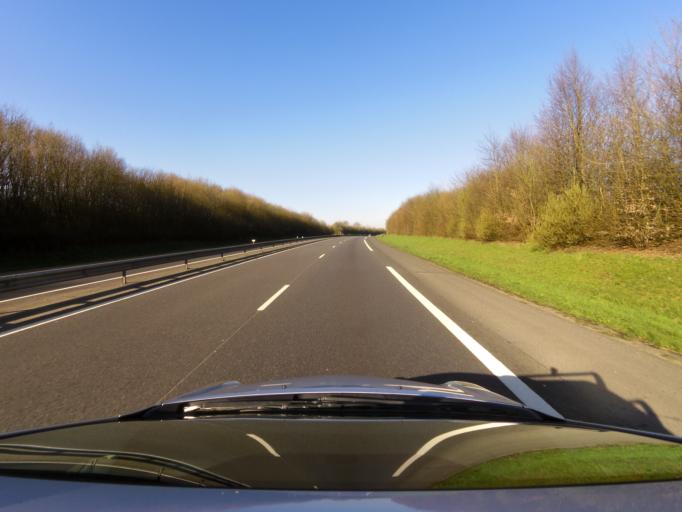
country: FR
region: Lower Normandy
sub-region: Departement du Calvados
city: Saint-Martin-des-Besaces
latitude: 49.0149
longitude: -0.8529
